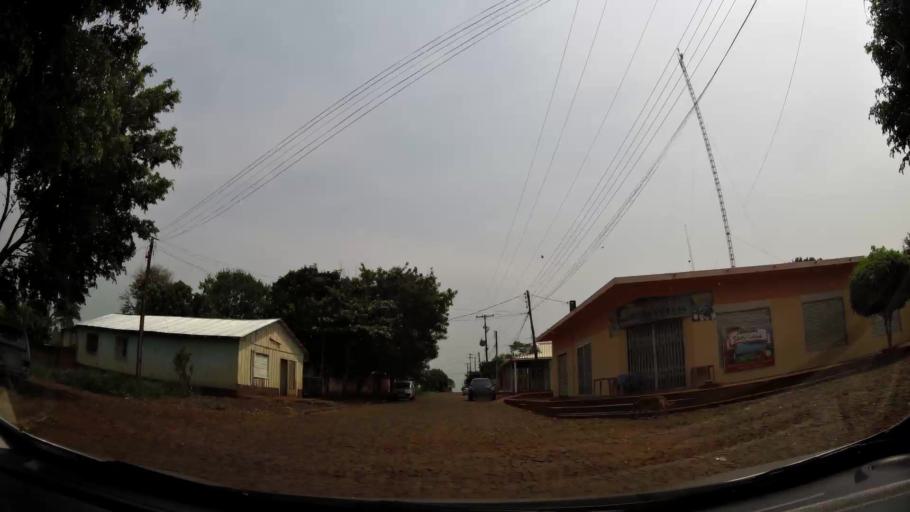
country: BR
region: Parana
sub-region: Foz Do Iguacu
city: Foz do Iguacu
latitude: -25.5695
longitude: -54.6094
